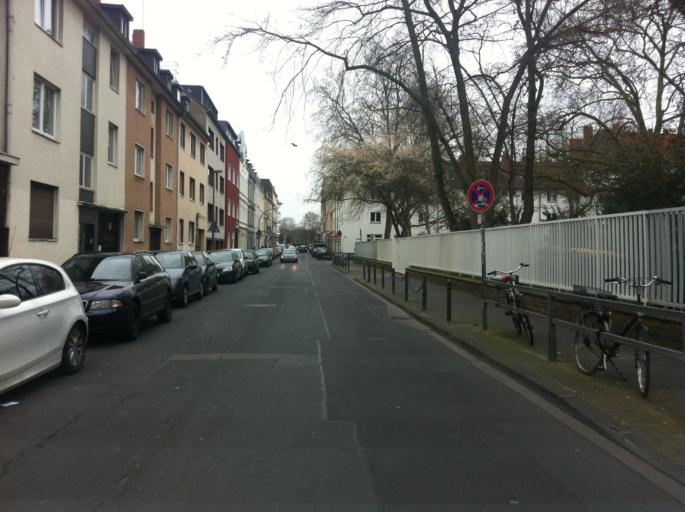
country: DE
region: North Rhine-Westphalia
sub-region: Regierungsbezirk Koln
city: Bilderstoeckchen
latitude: 50.9555
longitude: 6.9111
